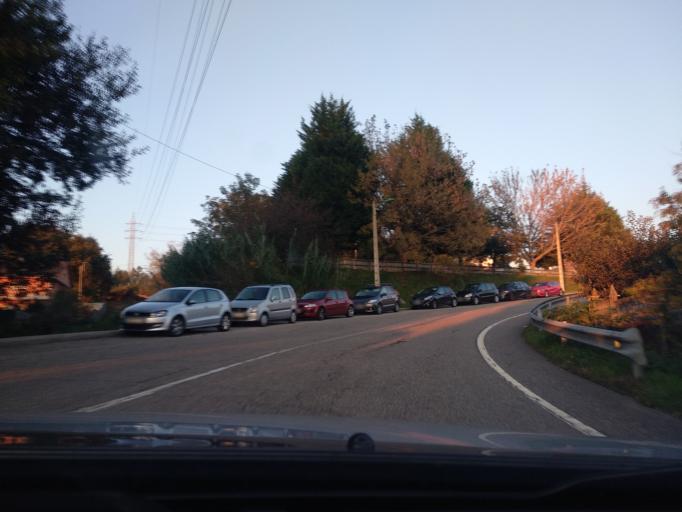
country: ES
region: Galicia
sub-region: Provincia de Pontevedra
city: Vigo
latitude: 42.2107
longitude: -8.6929
